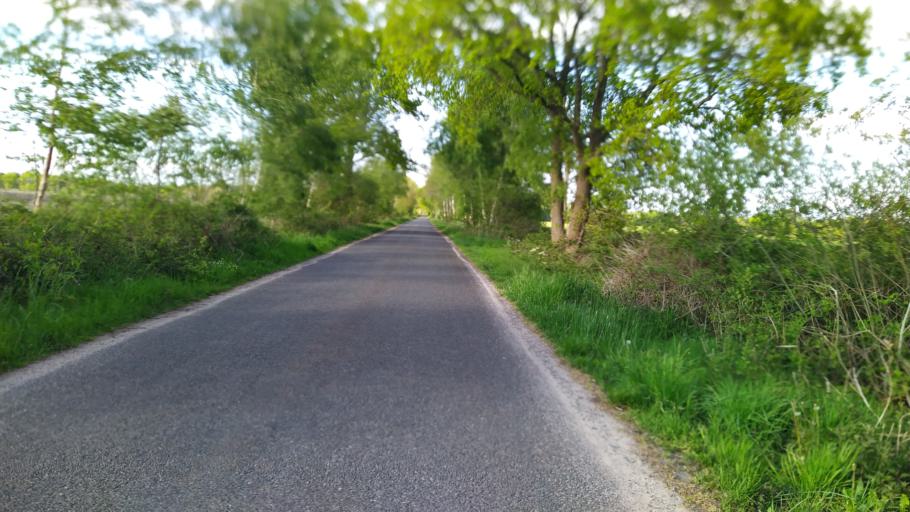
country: DE
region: Lower Saxony
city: Farven
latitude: 53.4218
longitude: 9.3360
